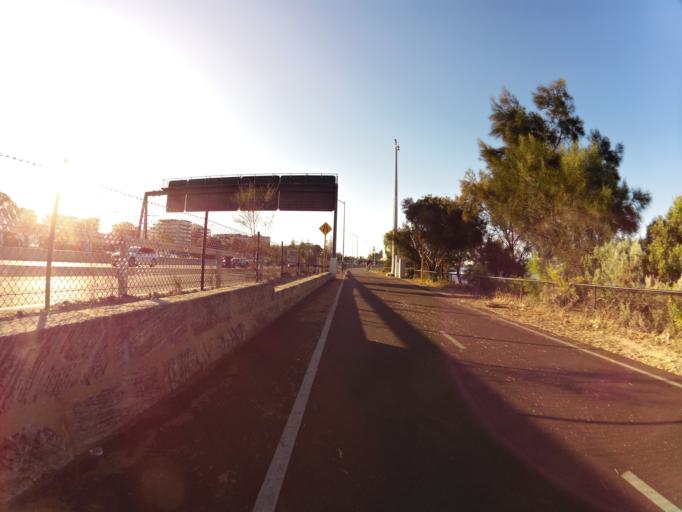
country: AU
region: Western Australia
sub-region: City of Perth
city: West Perth
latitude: -31.9695
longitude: 115.8464
